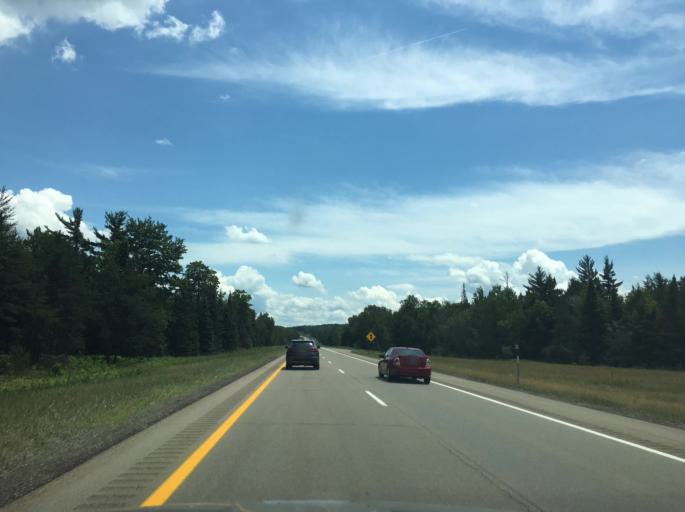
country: US
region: Michigan
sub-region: Roscommon County
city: Roscommon
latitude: 44.5083
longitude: -84.6594
